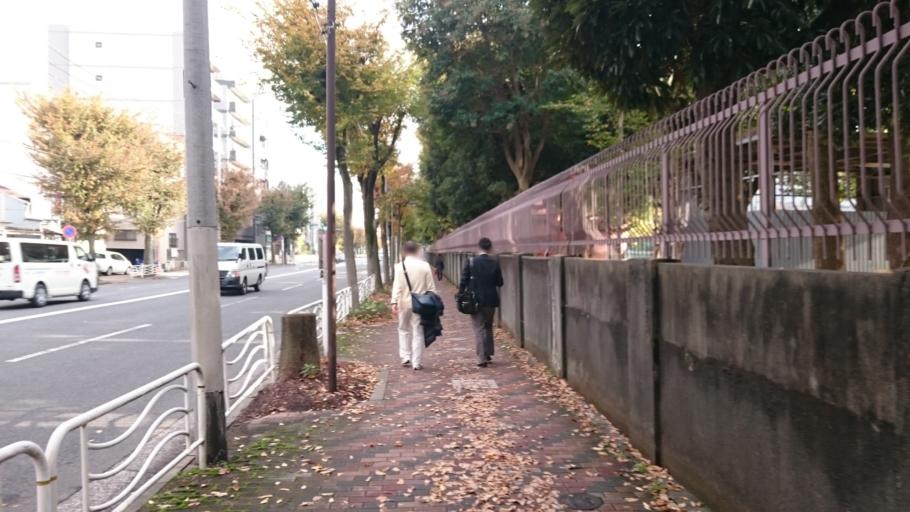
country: JP
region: Tokyo
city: Urayasu
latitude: 35.6668
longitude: 139.7940
